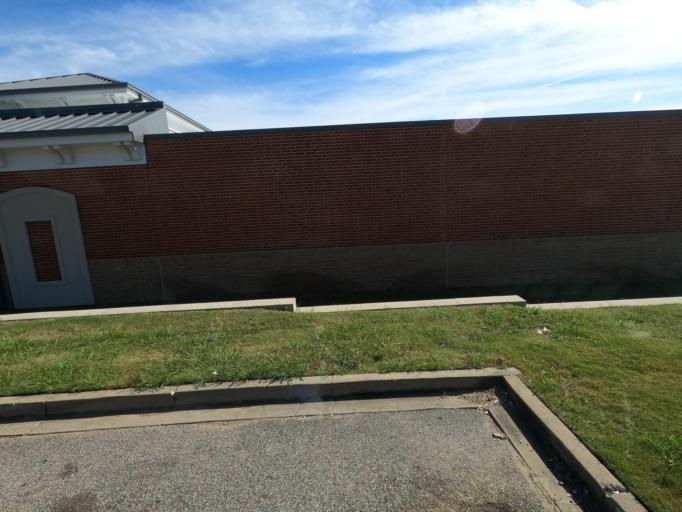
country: US
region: Tennessee
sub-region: Shelby County
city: Arlington
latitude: 35.2603
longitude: -89.6642
